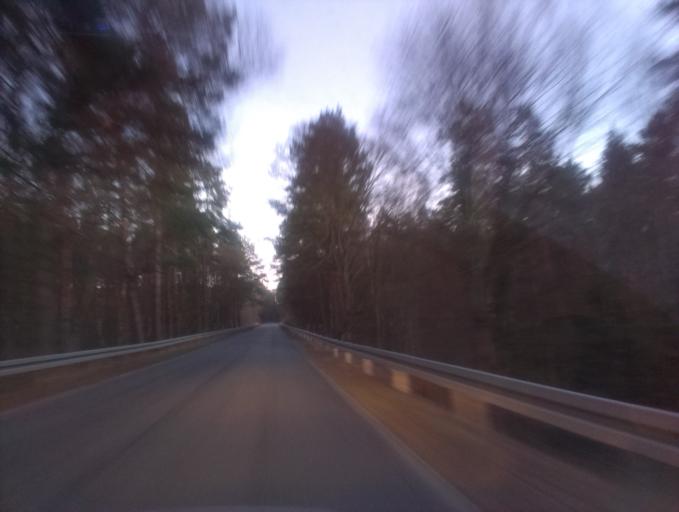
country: PL
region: Greater Poland Voivodeship
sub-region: Powiat zlotowski
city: Zlotow
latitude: 53.4910
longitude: 16.9867
